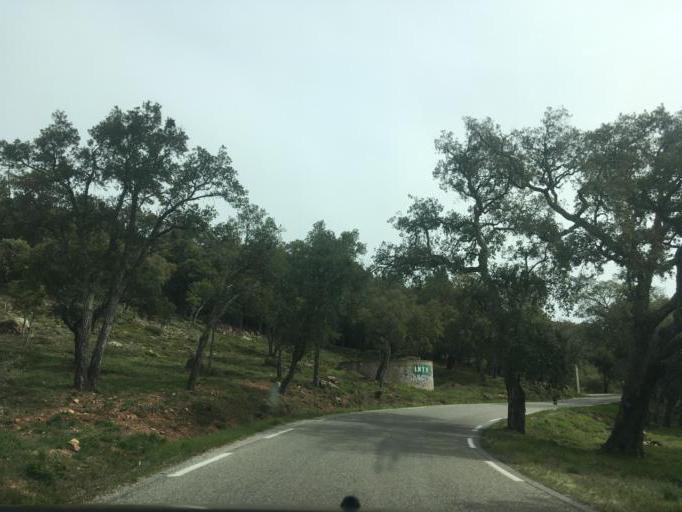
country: FR
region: Provence-Alpes-Cote d'Azur
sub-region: Departement du Var
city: Bagnols-en-Foret
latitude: 43.5161
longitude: 6.6308
